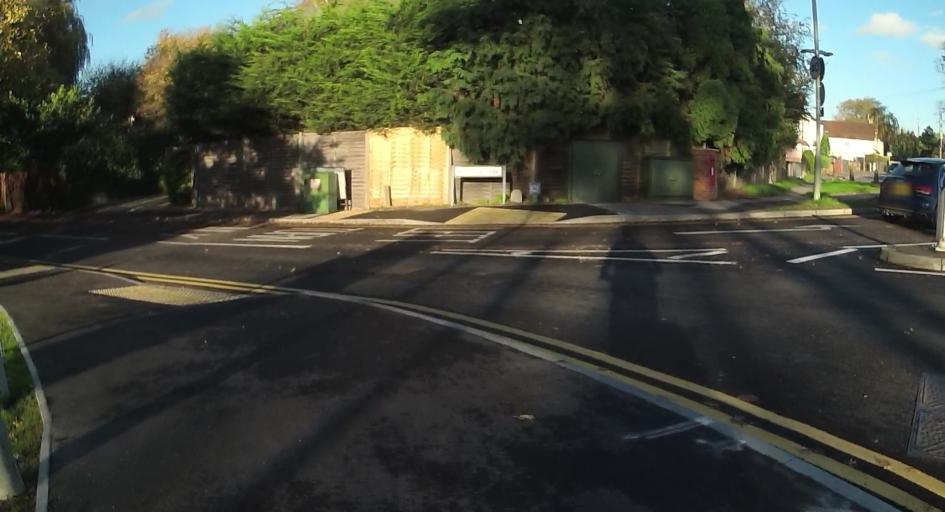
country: GB
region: England
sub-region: Bracknell Forest
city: Binfield
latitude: 51.4125
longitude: -0.8071
